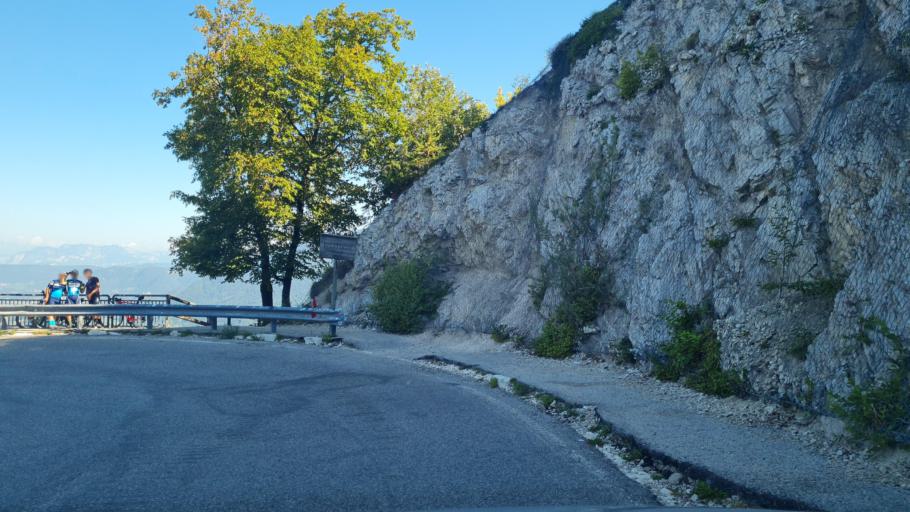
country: IT
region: Trentino-Alto Adige
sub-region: Provincia di Trento
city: Caldonazzo
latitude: 45.9761
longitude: 11.2901
